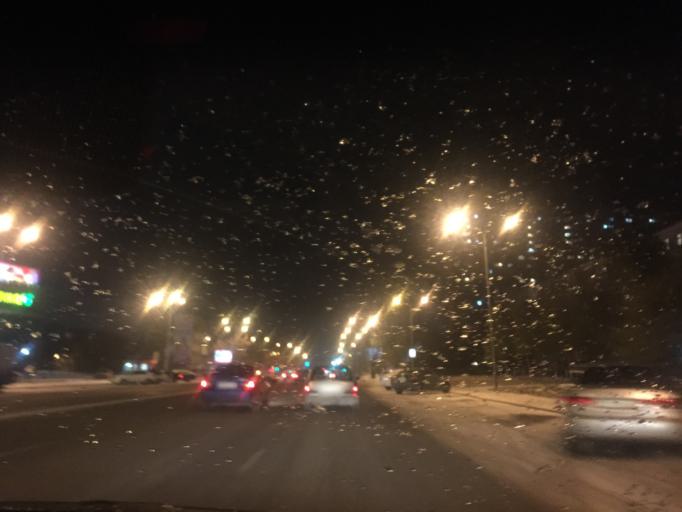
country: KZ
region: Astana Qalasy
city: Astana
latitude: 51.1744
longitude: 71.4247
